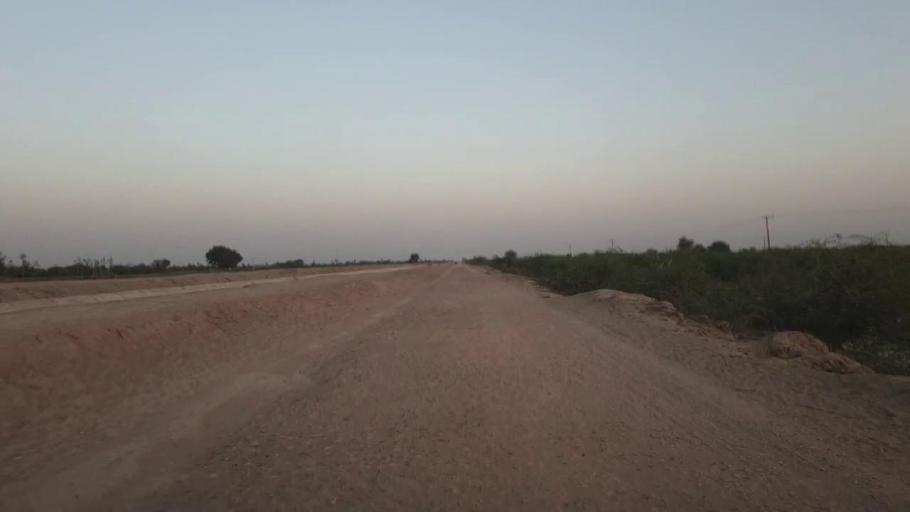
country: PK
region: Sindh
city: Dhoro Naro
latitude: 25.4410
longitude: 69.6363
